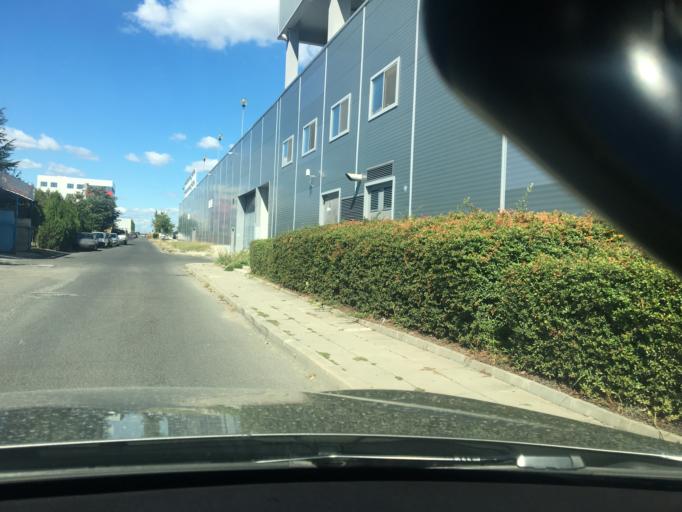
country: BG
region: Burgas
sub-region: Obshtina Burgas
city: Burgas
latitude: 42.5304
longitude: 27.4565
